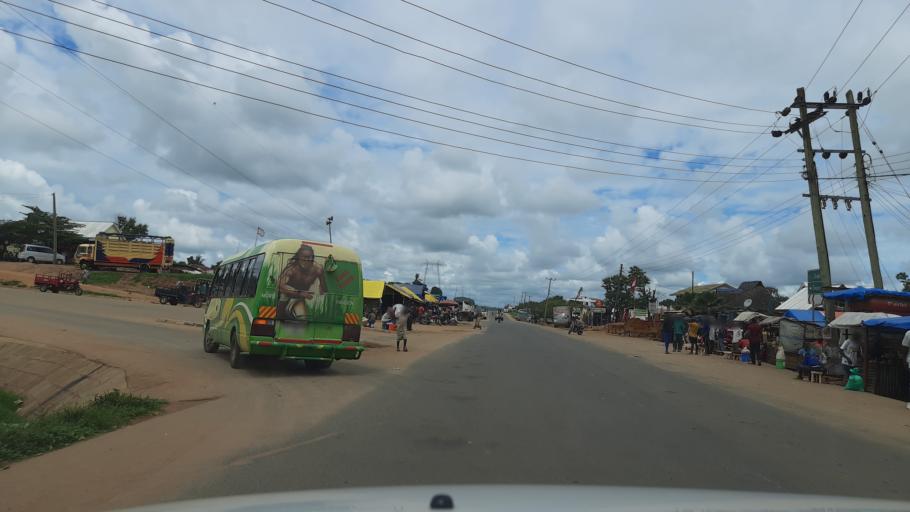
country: TZ
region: Tanga
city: Chanika
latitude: -5.7862
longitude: 38.2913
